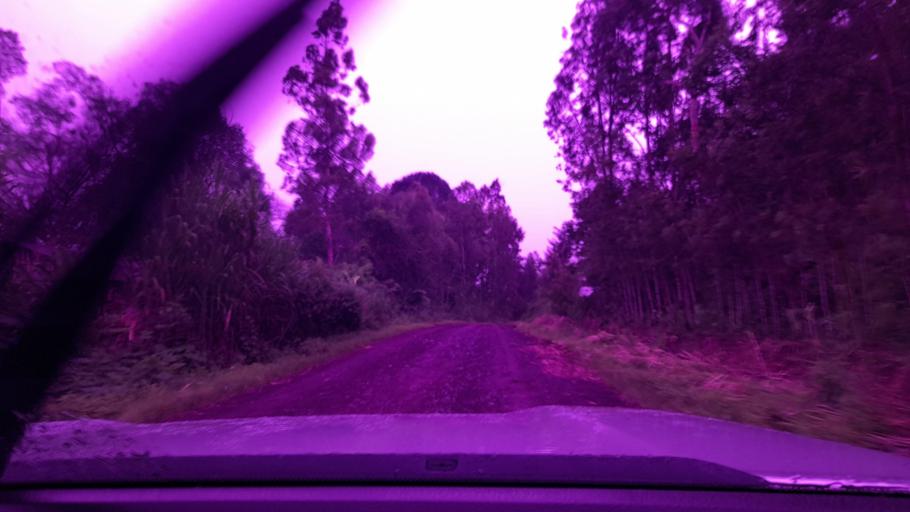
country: ET
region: Oromiya
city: Metu
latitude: 8.4557
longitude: 35.6372
